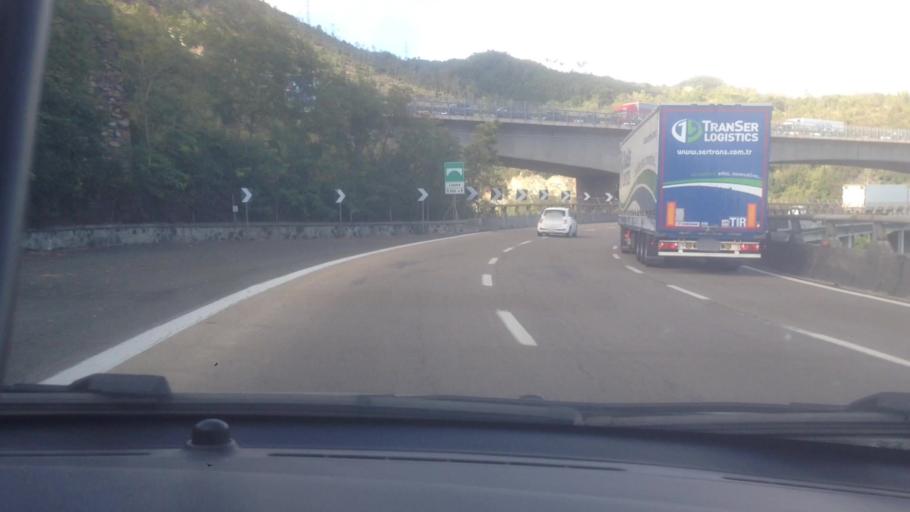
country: IT
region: Liguria
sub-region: Provincia di Genova
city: Arenzano
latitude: 44.4151
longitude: 8.7029
